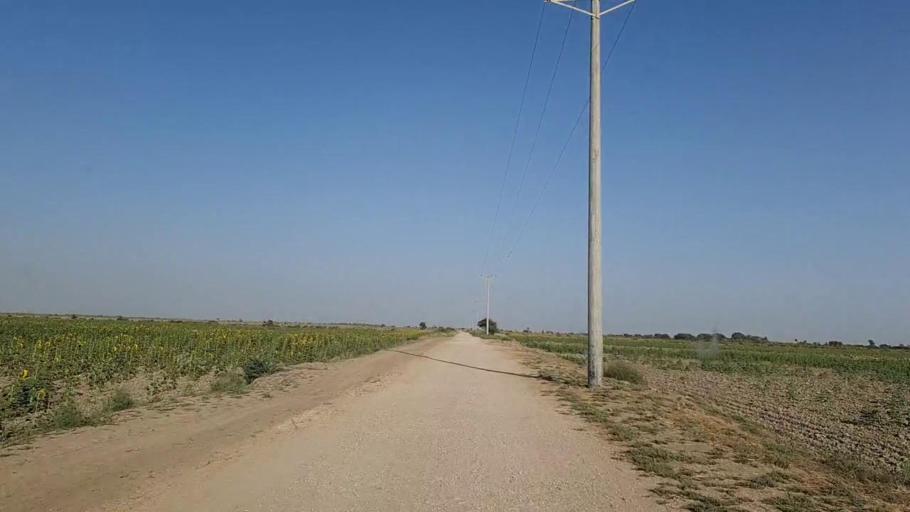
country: PK
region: Sindh
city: Jati
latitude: 24.4232
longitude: 68.2651
